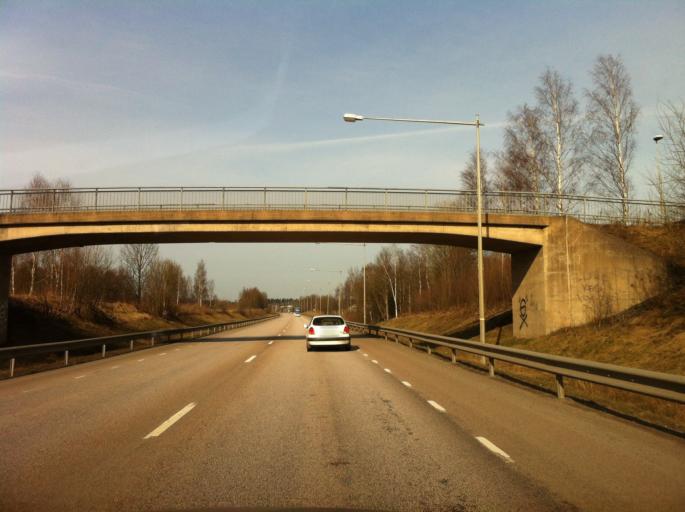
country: SE
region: Vaestra Goetaland
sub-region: Skovde Kommun
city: Skoevde
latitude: 58.3857
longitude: 13.8751
